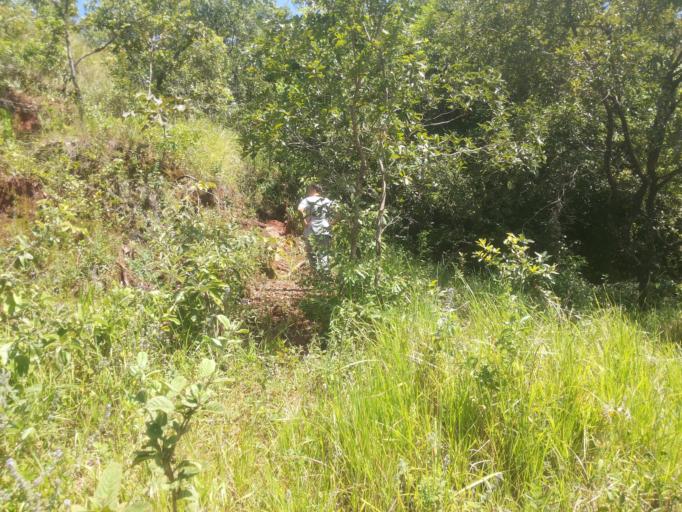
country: BR
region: Minas Gerais
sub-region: Ituiutaba
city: Ituiutaba
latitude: -19.0346
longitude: -49.4656
